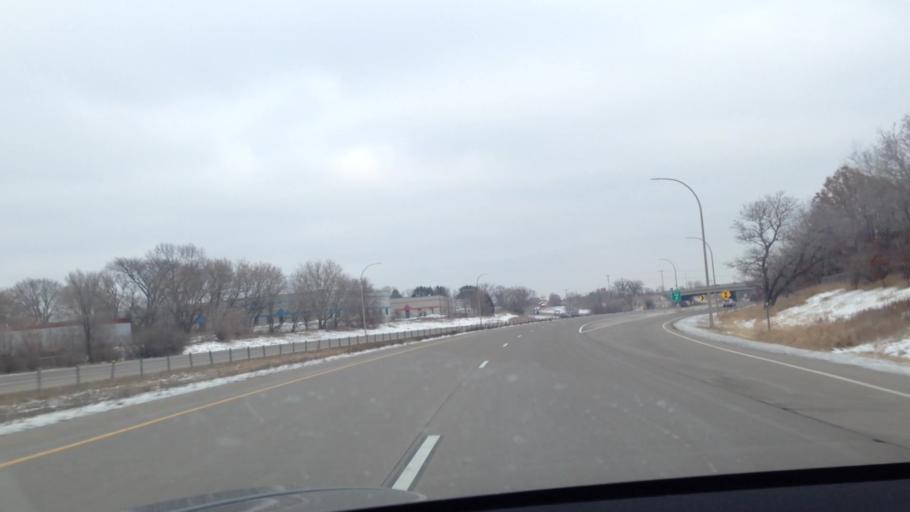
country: US
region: Minnesota
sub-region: Anoka County
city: Lino Lakes
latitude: 45.1779
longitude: -93.1180
